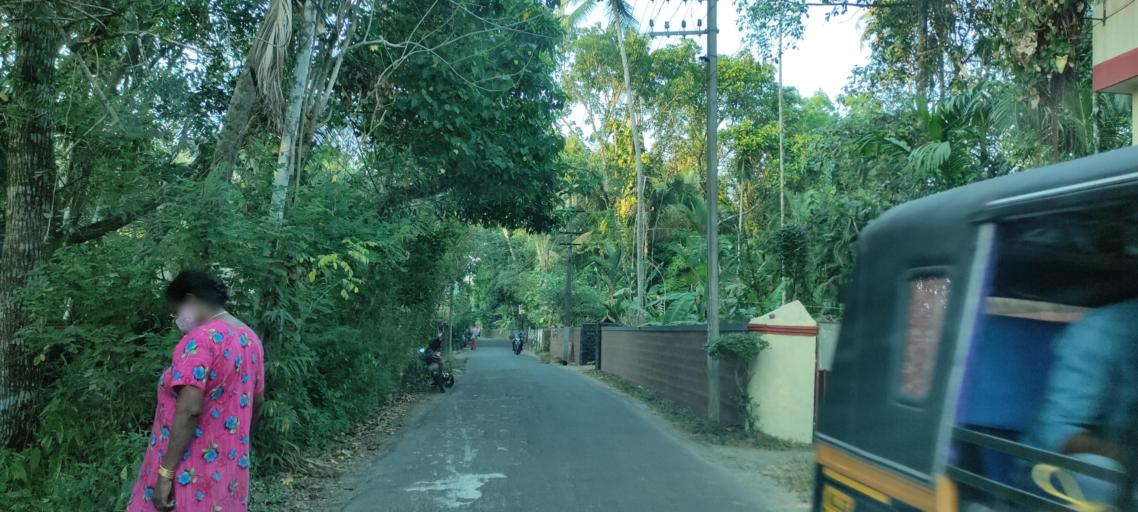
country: IN
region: Kerala
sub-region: Alappuzha
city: Kutiatodu
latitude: 9.7768
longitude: 76.3251
